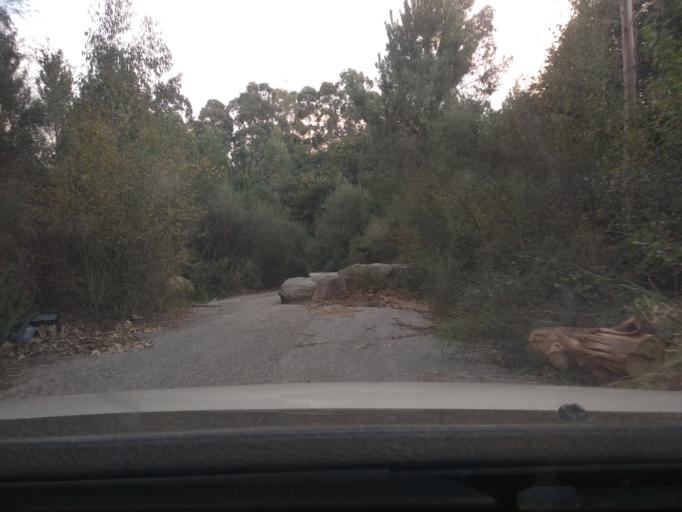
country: ES
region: Galicia
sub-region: Provincia de Pontevedra
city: Moana
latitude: 42.3018
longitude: -8.6960
